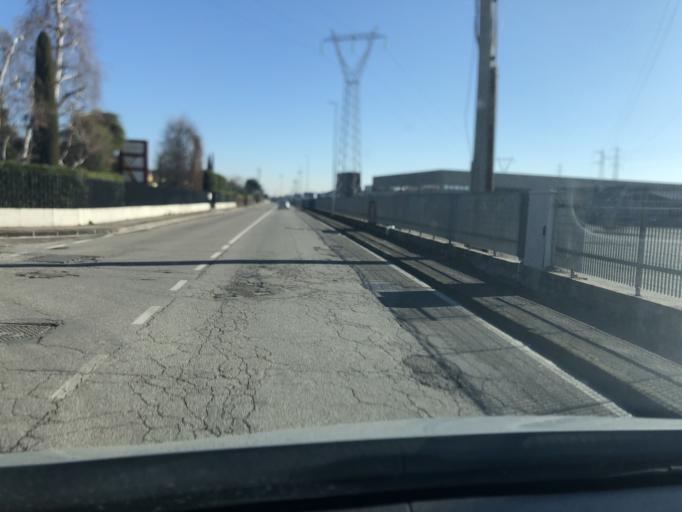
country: IT
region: Veneto
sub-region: Provincia di Verona
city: Lugagnano
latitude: 45.4482
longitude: 10.8710
